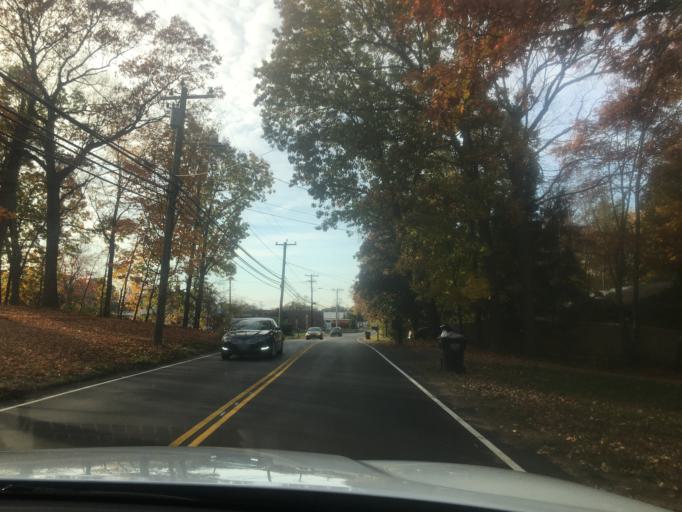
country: US
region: Connecticut
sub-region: Hartford County
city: South Windsor
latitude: 41.8180
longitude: -72.6049
